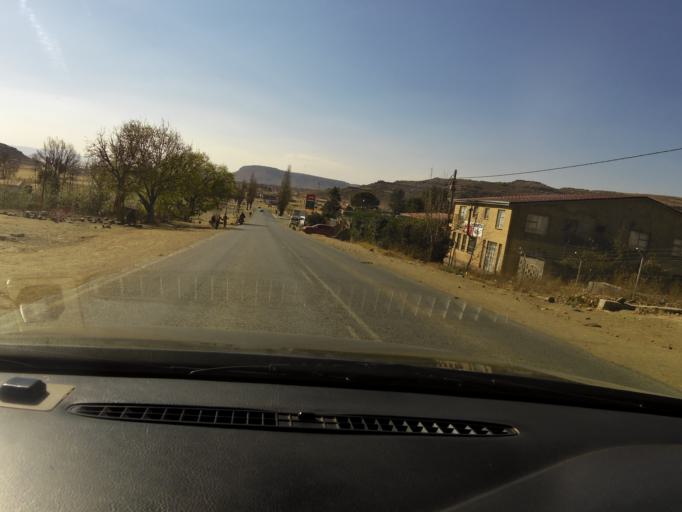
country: LS
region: Mohale's Hoek District
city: Mohale's Hoek
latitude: -30.1497
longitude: 27.4760
